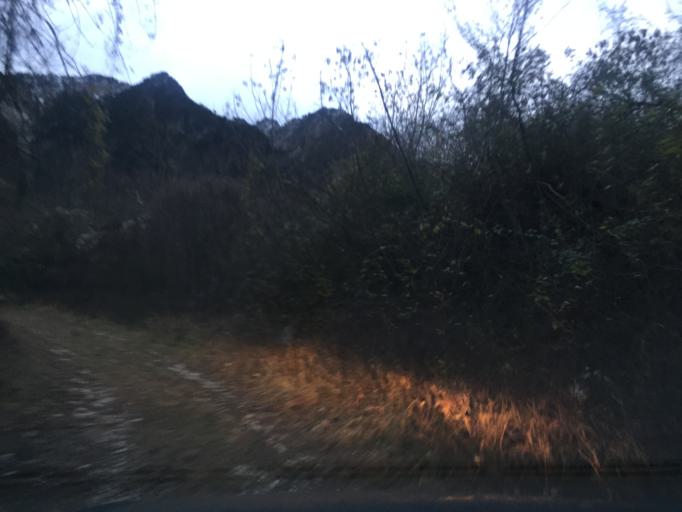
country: IT
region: Friuli Venezia Giulia
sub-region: Provincia di Udine
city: Venzone
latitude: 46.3208
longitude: 13.1402
